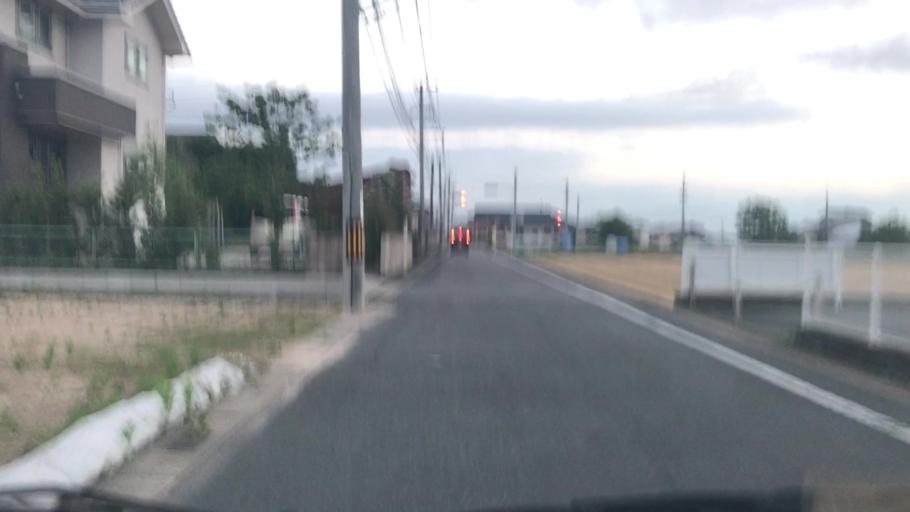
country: JP
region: Saga Prefecture
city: Saga-shi
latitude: 33.2290
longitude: 130.3020
